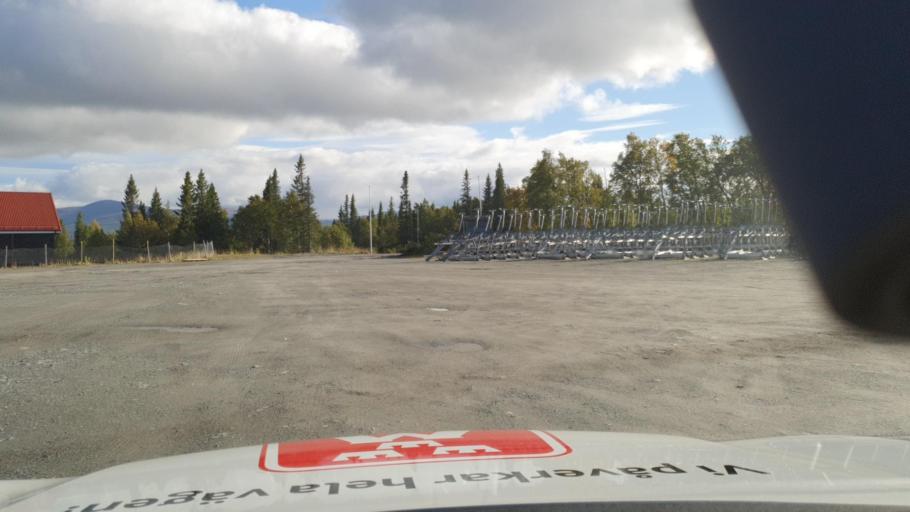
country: SE
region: Jaemtland
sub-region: Are Kommun
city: Are
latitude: 63.2663
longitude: 13.1613
